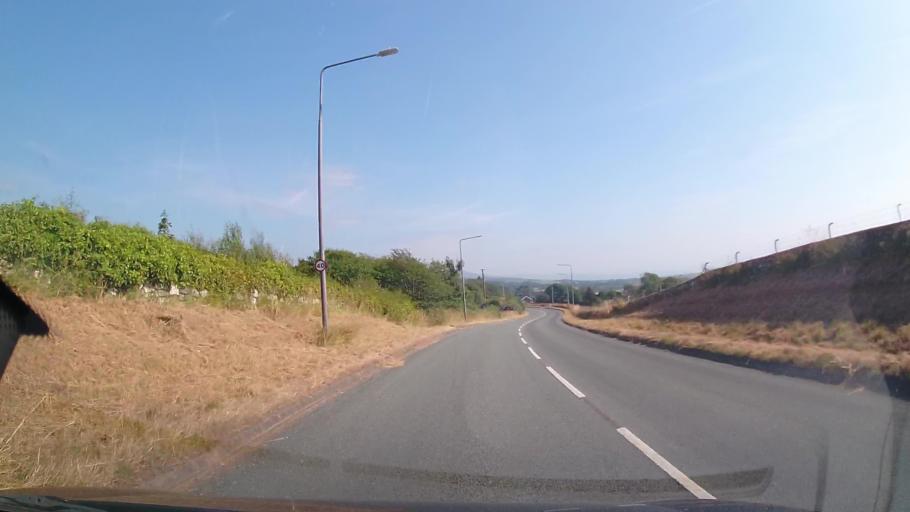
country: GB
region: Wales
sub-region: Gwynedd
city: Llanfair
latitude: 52.8415
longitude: -4.1152
